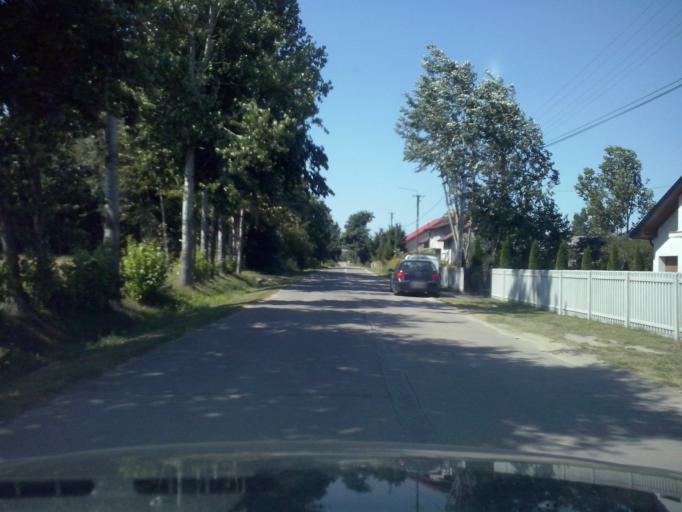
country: PL
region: Swietokrzyskie
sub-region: Powiat buski
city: Gnojno
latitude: 50.6003
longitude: 20.8026
